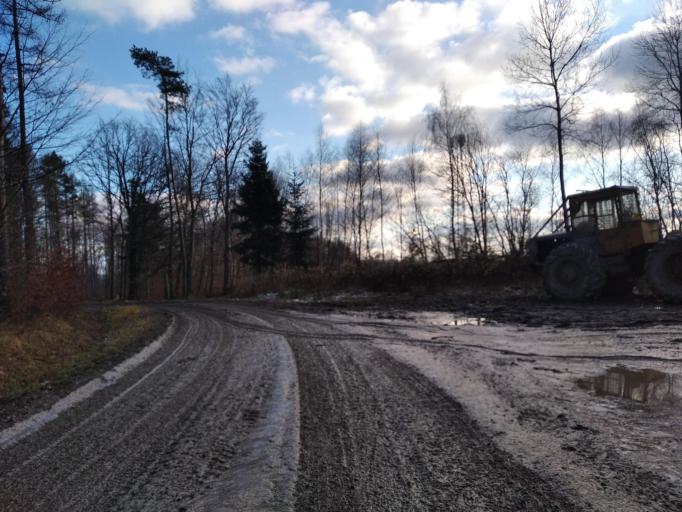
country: PL
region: Subcarpathian Voivodeship
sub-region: Powiat strzyzowski
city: Babica
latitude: 49.9508
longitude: 21.8703
